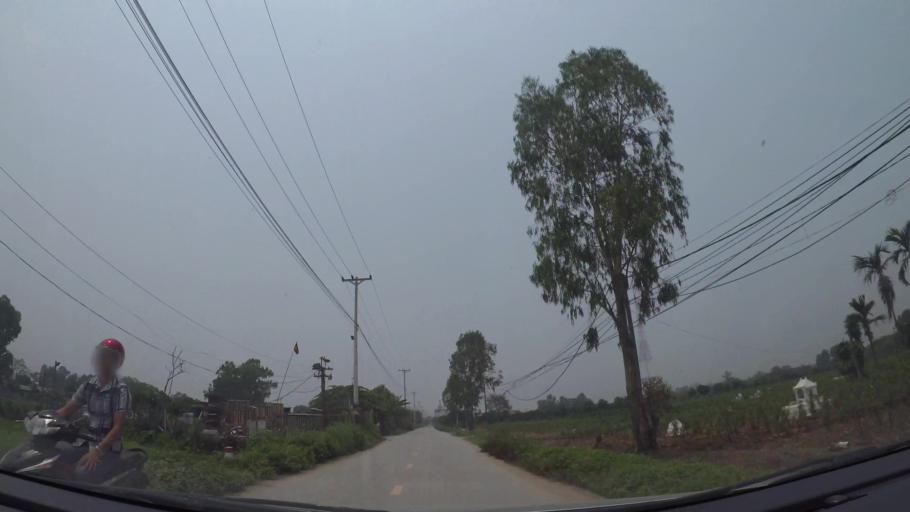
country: VN
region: Ha Noi
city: Ha Dong
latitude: 20.9970
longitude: 105.7691
